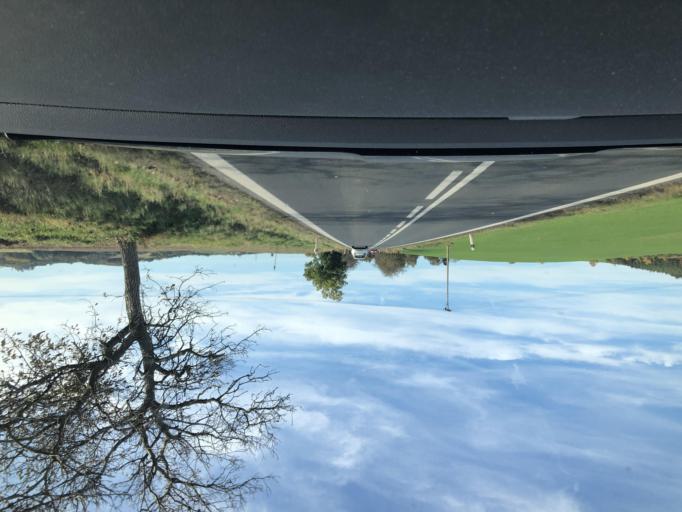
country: CZ
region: Central Bohemia
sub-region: Okres Benesov
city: Benesov
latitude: 49.7713
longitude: 14.7298
